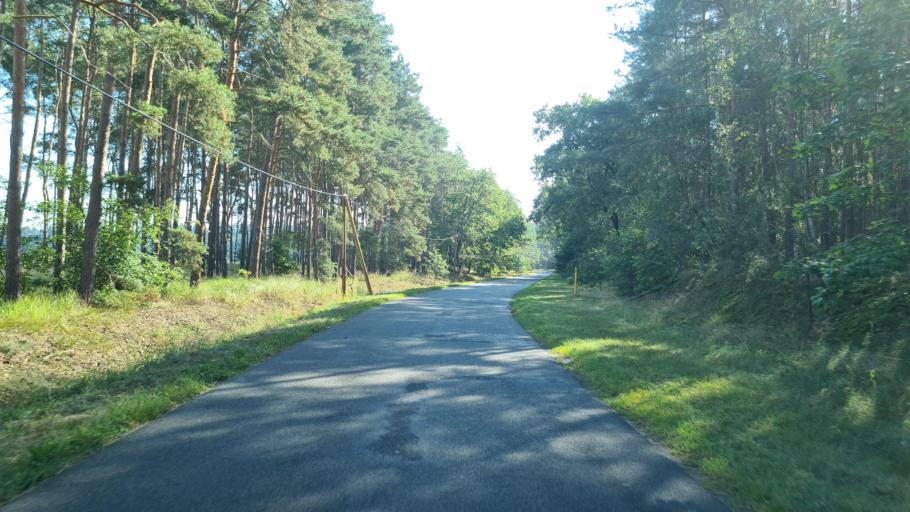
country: DE
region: Brandenburg
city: Friesack
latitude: 52.7789
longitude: 12.6167
